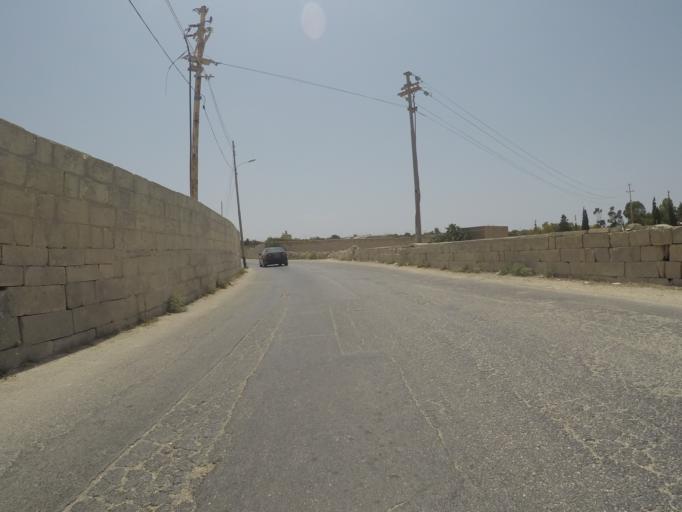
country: MT
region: Is-Siggiewi
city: Siggiewi
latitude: 35.8458
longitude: 14.4336
